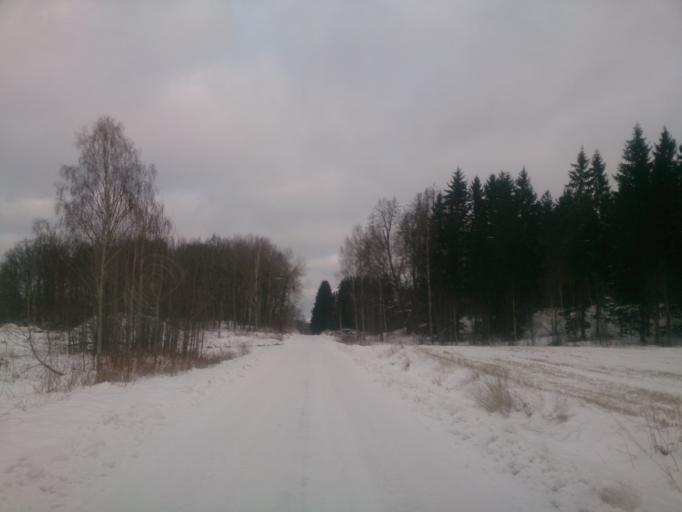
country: SE
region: OEstergoetland
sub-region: Atvidabergs Kommun
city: Atvidaberg
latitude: 58.2171
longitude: 15.9895
